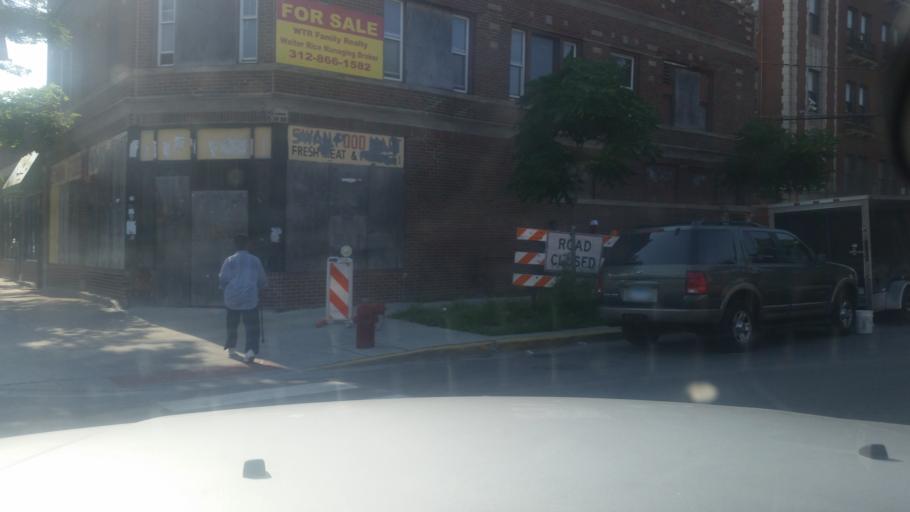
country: US
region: Illinois
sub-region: Cook County
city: Chicago
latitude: 41.7663
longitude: -87.5724
